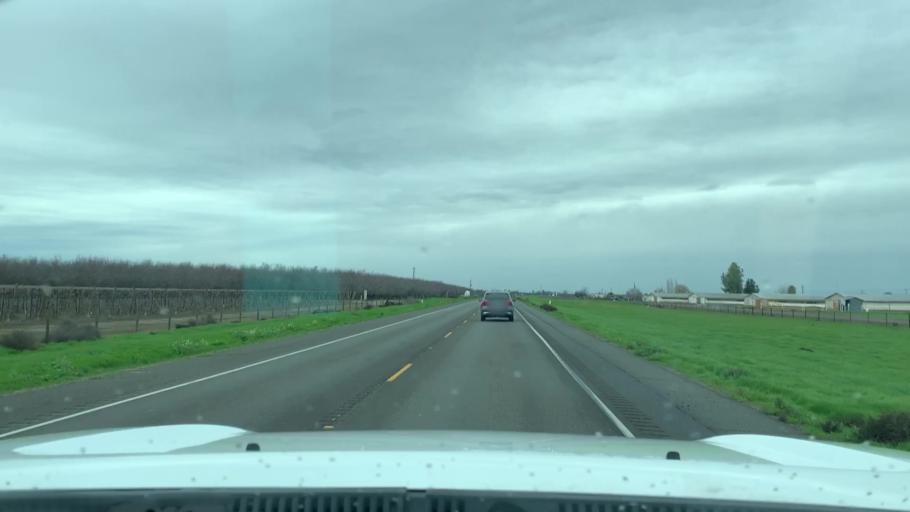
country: US
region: California
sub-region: Fresno County
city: Caruthers
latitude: 36.4771
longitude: -119.7930
